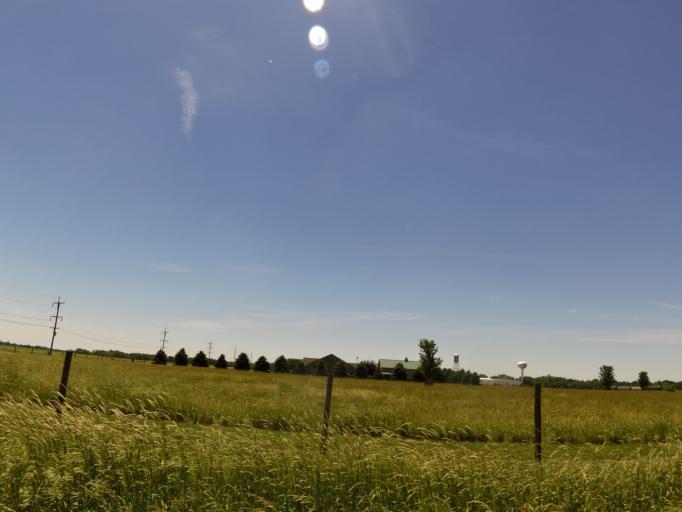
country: US
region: Illinois
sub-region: Iroquois County
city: Milford
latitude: 40.6394
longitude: -87.6921
